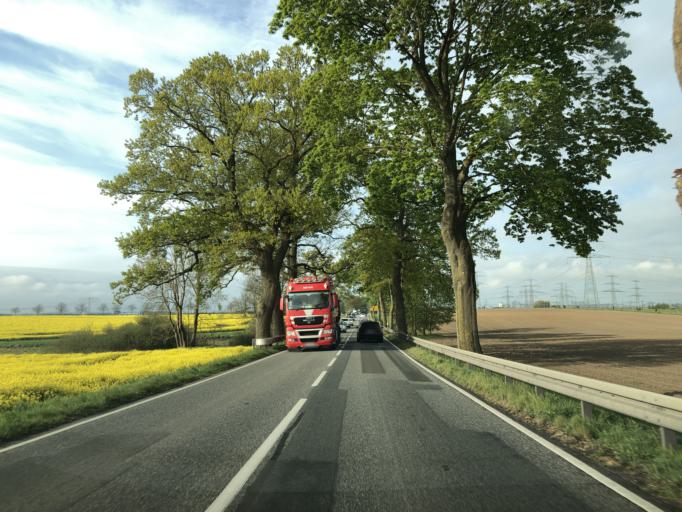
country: DE
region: Mecklenburg-Vorpommern
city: Guestrow
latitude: 53.8246
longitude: 12.2022
